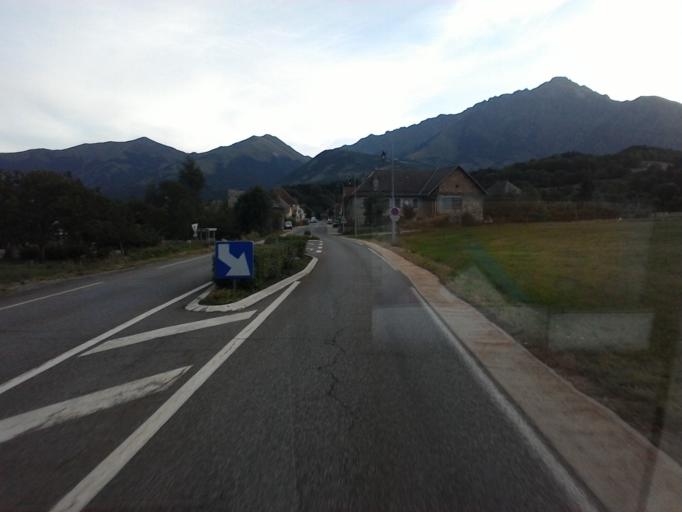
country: FR
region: Provence-Alpes-Cote d'Azur
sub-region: Departement des Hautes-Alpes
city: Saint-Bonnet-en-Champsaur
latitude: 44.7505
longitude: 6.0085
